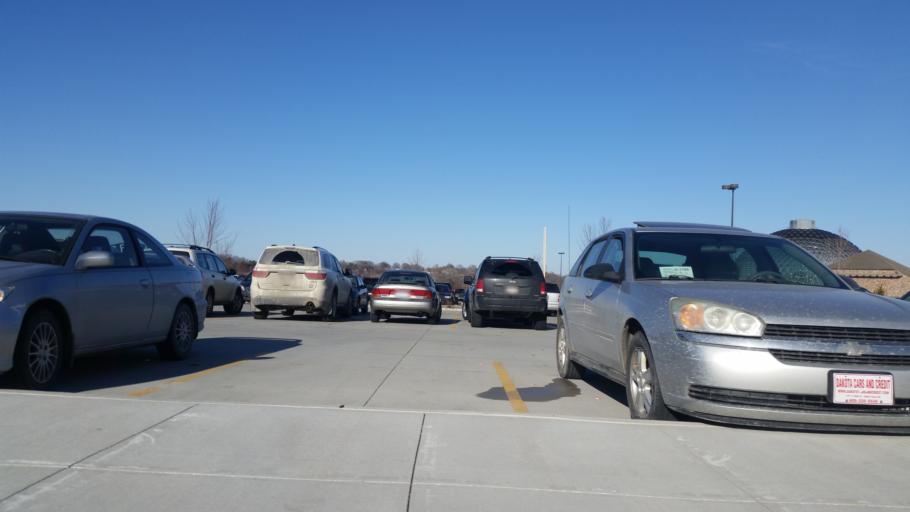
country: US
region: Nebraska
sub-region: Douglas County
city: Omaha
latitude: 41.2244
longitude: -95.9321
